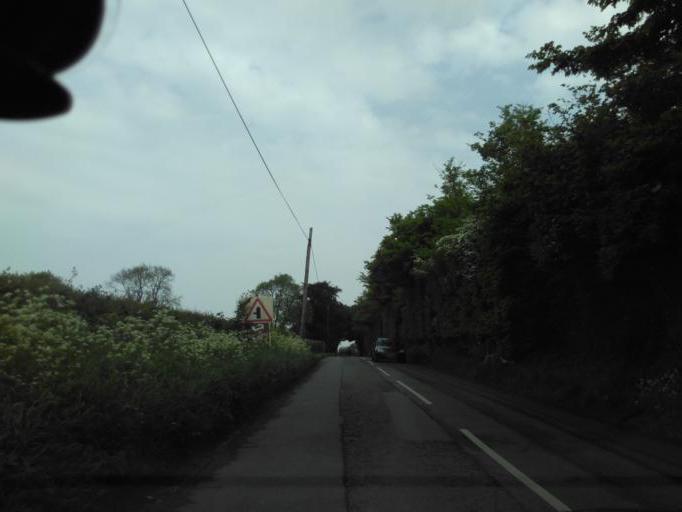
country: GB
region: England
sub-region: Kent
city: Lyminge
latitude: 51.1639
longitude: 1.0519
